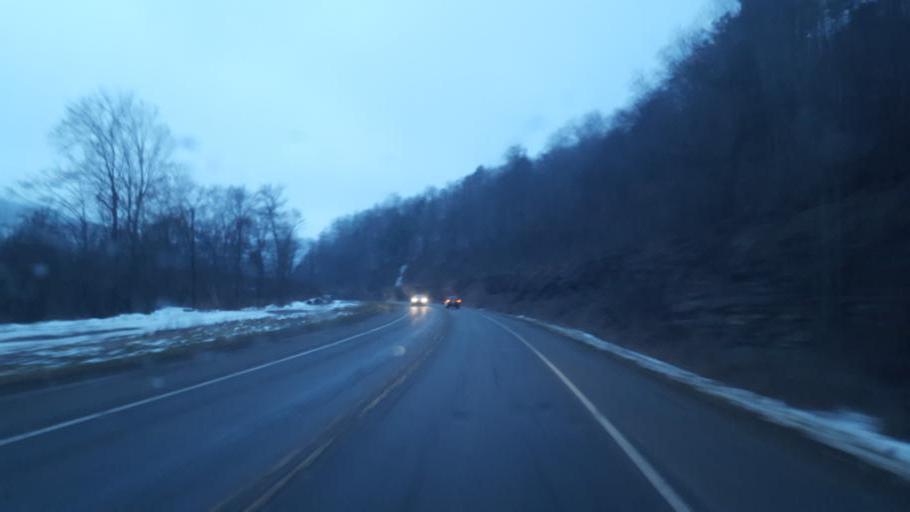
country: US
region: Pennsylvania
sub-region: McKean County
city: Port Allegany
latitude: 41.7915
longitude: -78.1937
